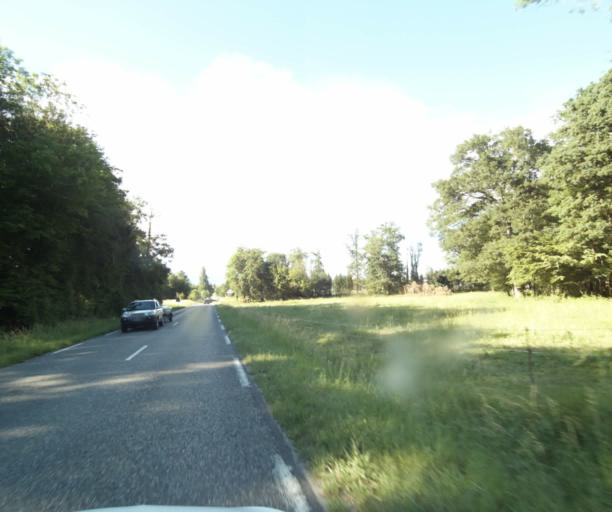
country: FR
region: Rhone-Alpes
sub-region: Departement de la Haute-Savoie
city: Messery
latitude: 46.3406
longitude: 6.2919
